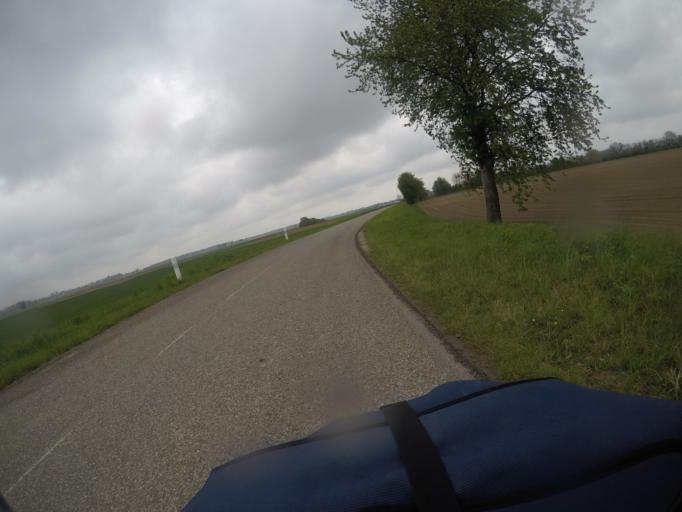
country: FR
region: Alsace
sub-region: Departement du Bas-Rhin
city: Roppenheim
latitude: 48.8235
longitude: 8.0662
